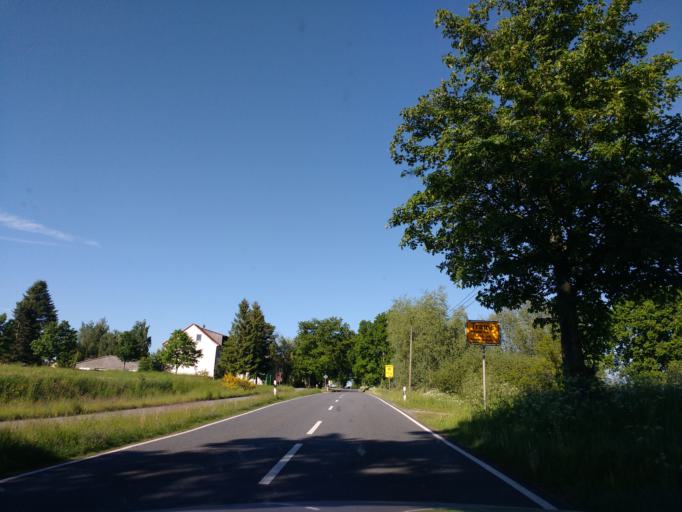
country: DE
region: Mecklenburg-Vorpommern
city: Zurow
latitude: 53.8082
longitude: 11.6119
